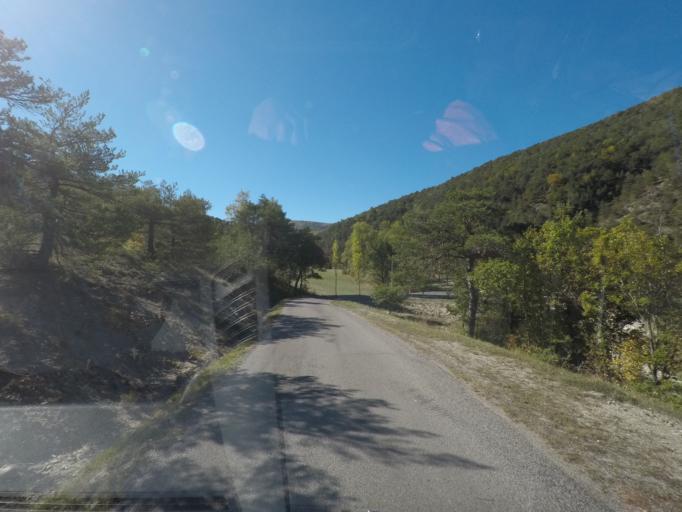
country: FR
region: Rhone-Alpes
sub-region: Departement de la Drome
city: Die
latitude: 44.5554
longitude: 5.3251
